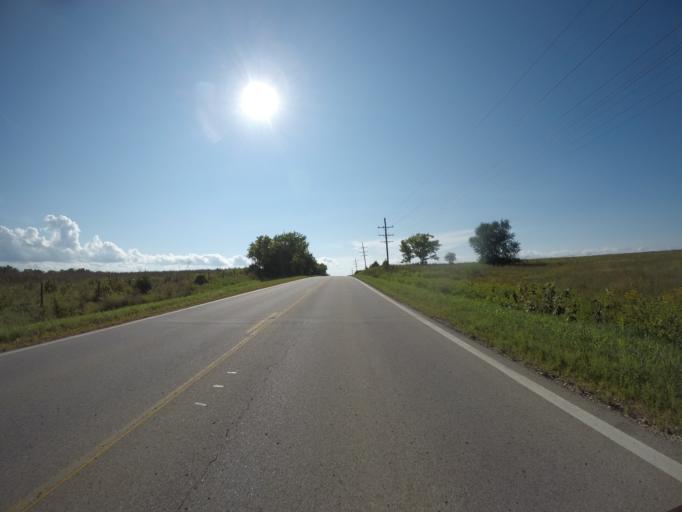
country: US
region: Kansas
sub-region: Leavenworth County
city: Tonganoxie
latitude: 39.1434
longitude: -95.1389
